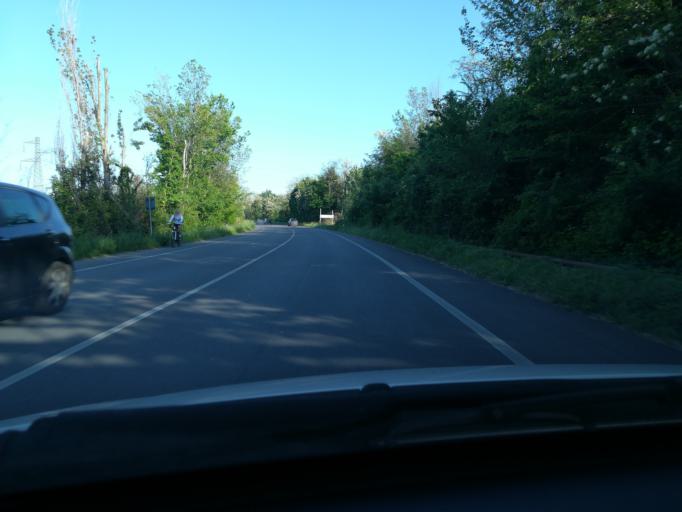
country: IT
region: Emilia-Romagna
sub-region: Provincia di Rimini
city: Montalbano
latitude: 43.9598
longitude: 12.7150
